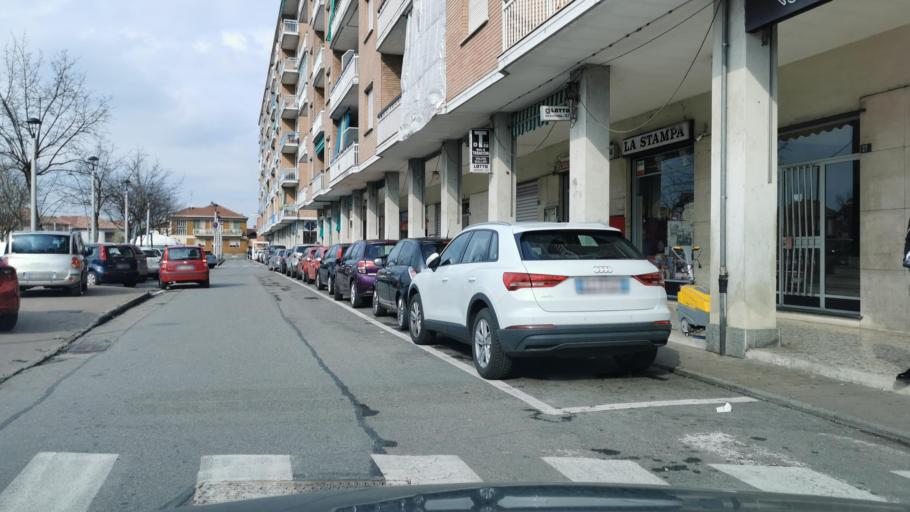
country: IT
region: Piedmont
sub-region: Provincia di Torino
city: Volpiano
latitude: 45.2002
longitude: 7.7821
